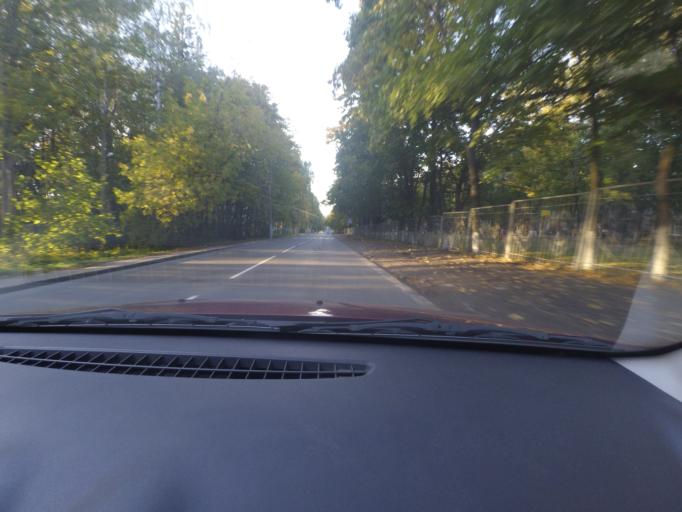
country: RU
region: Nizjnij Novgorod
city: Nizhniy Novgorod
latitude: 56.2635
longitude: 43.9996
